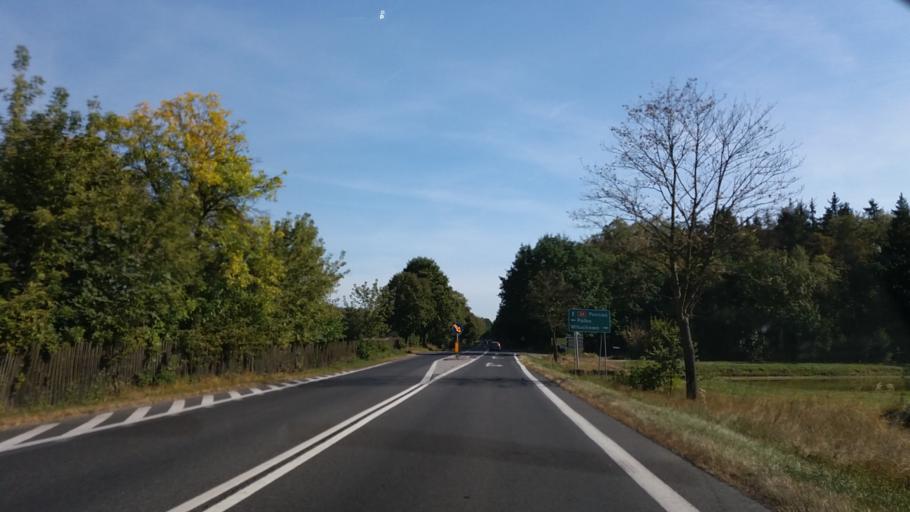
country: PL
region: Greater Poland Voivodeship
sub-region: Powiat miedzychodzki
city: Kwilcz
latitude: 52.5438
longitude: 16.1250
